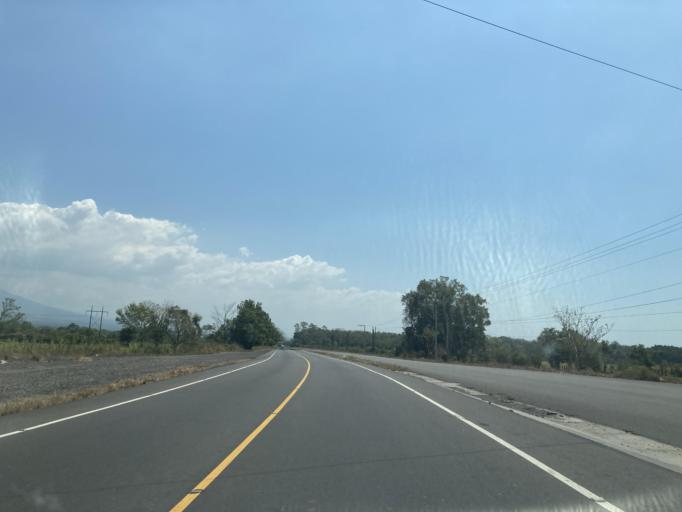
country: GT
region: Escuintla
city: Guanagazapa
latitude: 14.1071
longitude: -90.6297
